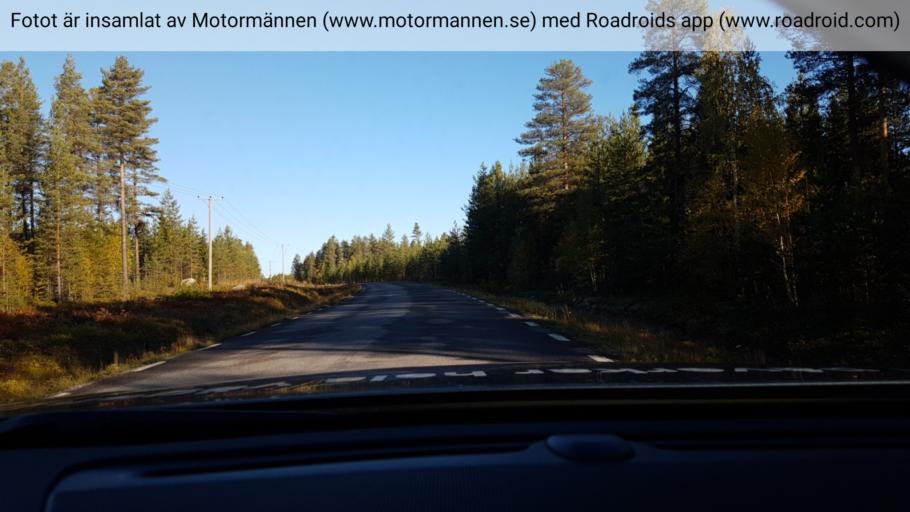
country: SE
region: Norrbotten
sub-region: Bodens Kommun
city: Boden
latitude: 65.9287
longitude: 21.6525
